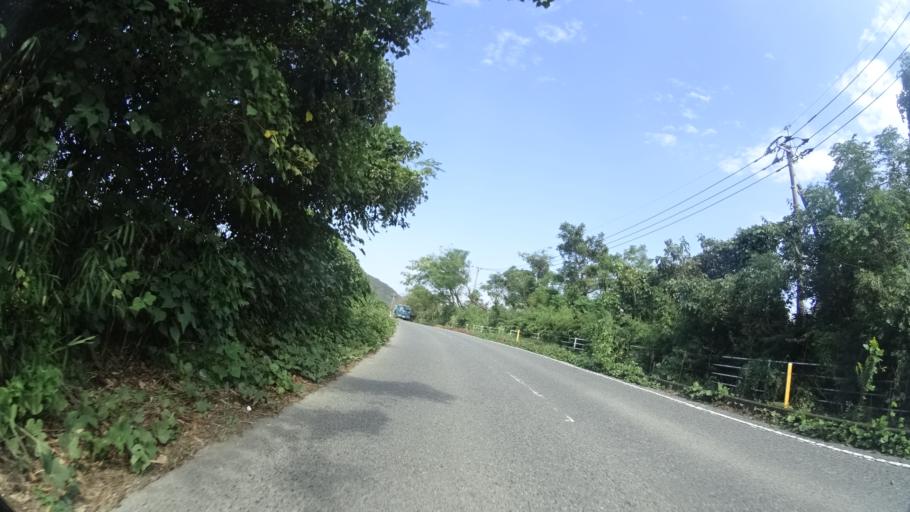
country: JP
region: Kumamoto
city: Uto
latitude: 32.6682
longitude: 130.7189
